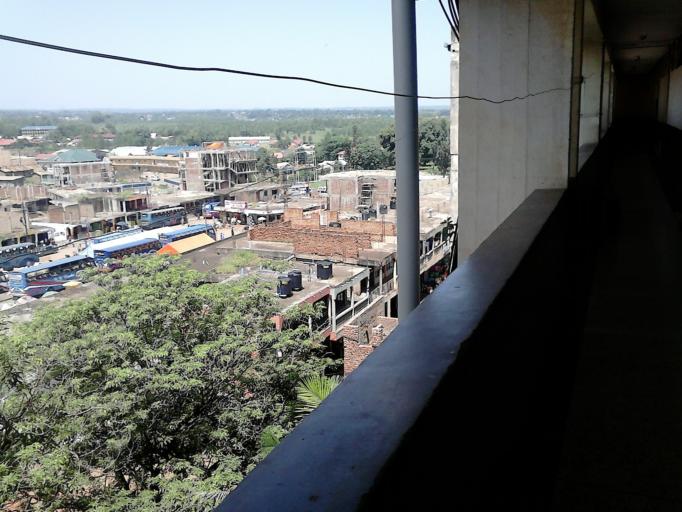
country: UG
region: Eastern Region
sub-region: Mbale District
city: Mbale
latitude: 1.0720
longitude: 34.1751
